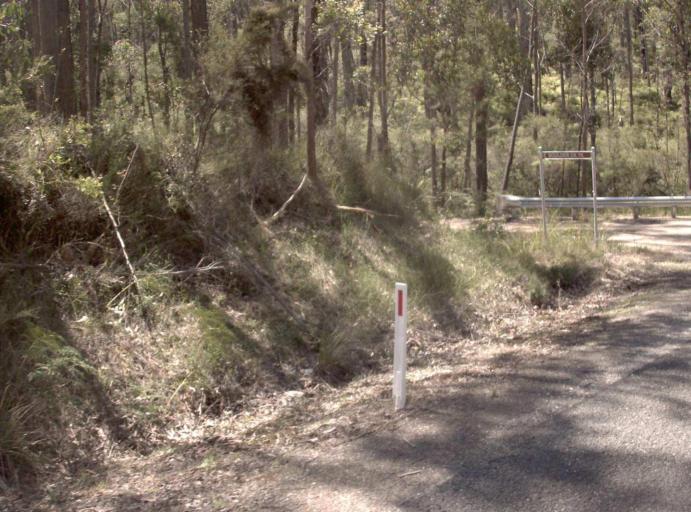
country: AU
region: New South Wales
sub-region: Bombala
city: Bombala
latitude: -37.6123
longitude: 148.8892
